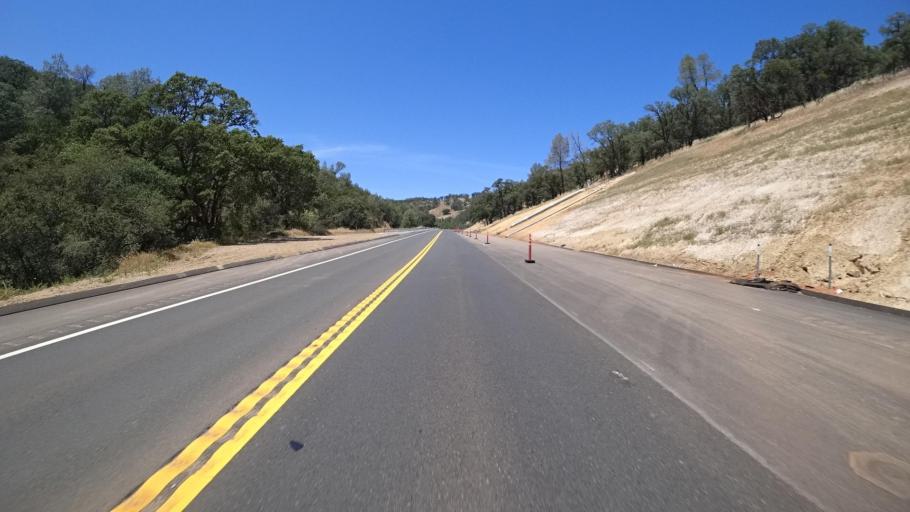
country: US
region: California
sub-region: Lake County
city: Hidden Valley Lake
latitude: 38.8308
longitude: -122.5862
